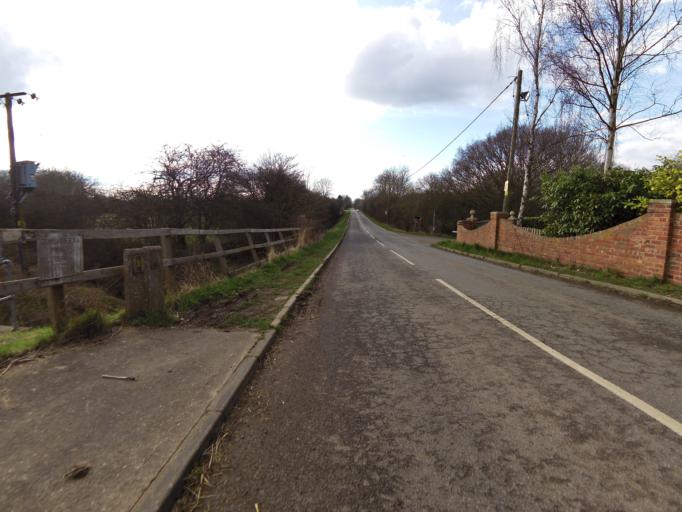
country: GB
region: England
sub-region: East Riding of Yorkshire
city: Snaith
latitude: 53.6484
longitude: -1.0271
